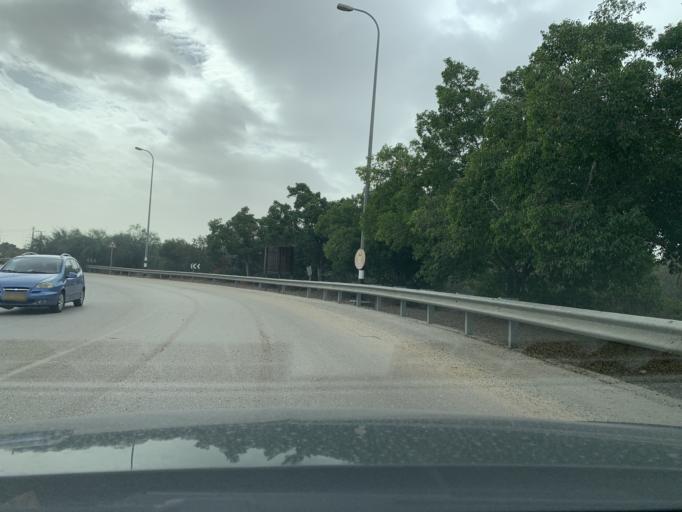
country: IL
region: Central District
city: Jaljulya
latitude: 32.1552
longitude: 34.9465
